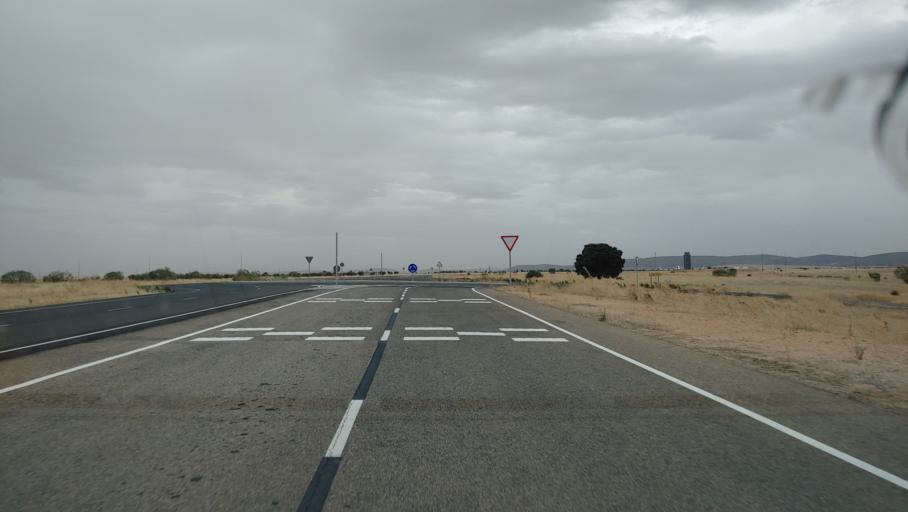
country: ES
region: Castille-La Mancha
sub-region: Provincia de Ciudad Real
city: Villar del Pozo
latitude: 38.8712
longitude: -3.9877
